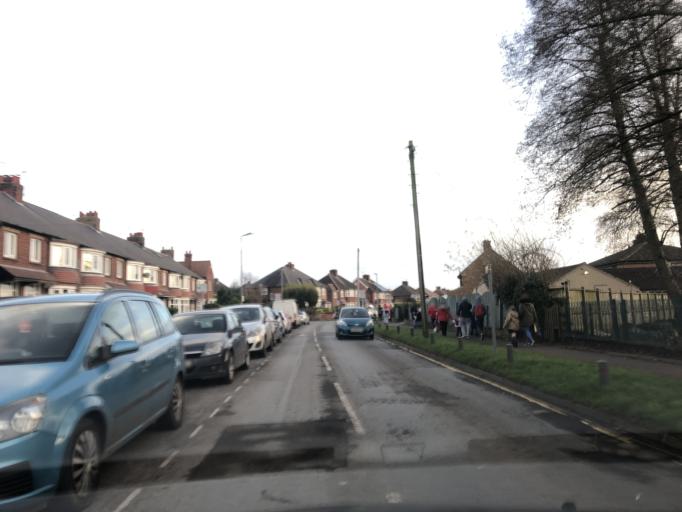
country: GB
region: England
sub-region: North Yorkshire
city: Northallerton
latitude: 54.3369
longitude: -1.4285
